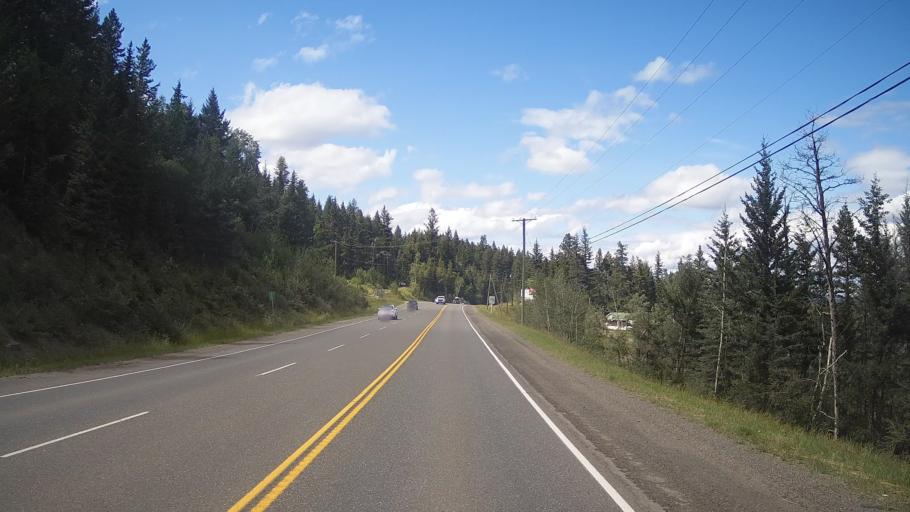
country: CA
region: British Columbia
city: Cache Creek
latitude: 51.6240
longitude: -121.2969
